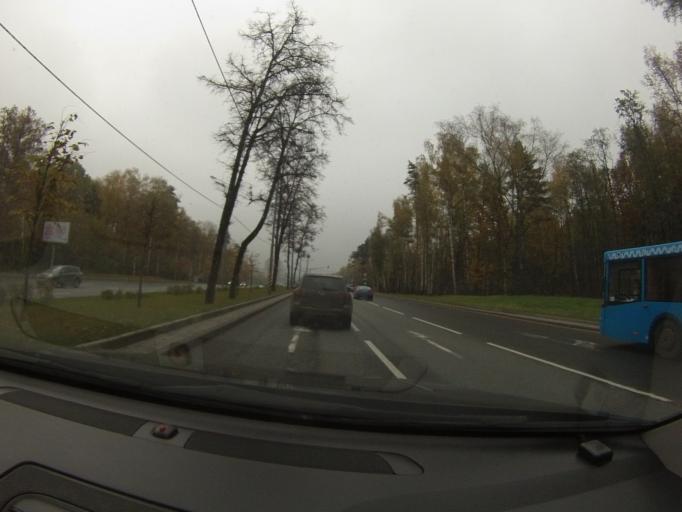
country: RU
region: Moscow
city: Rublevo
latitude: 55.7586
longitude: 37.3934
